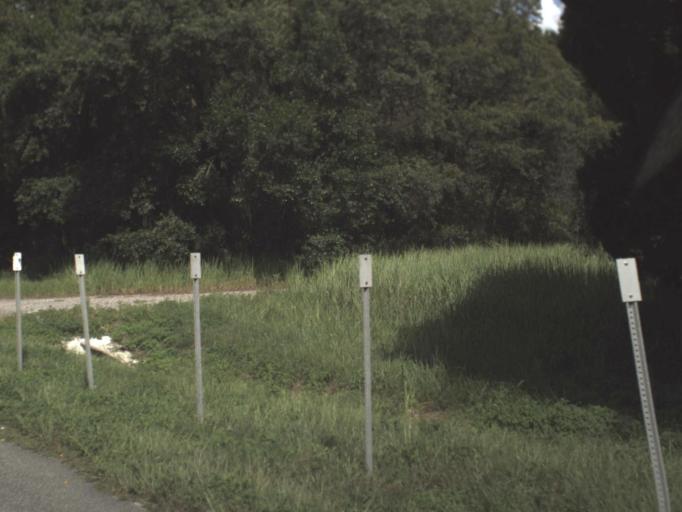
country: US
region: Florida
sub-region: Pasco County
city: Dade City
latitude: 28.3438
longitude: -82.2240
